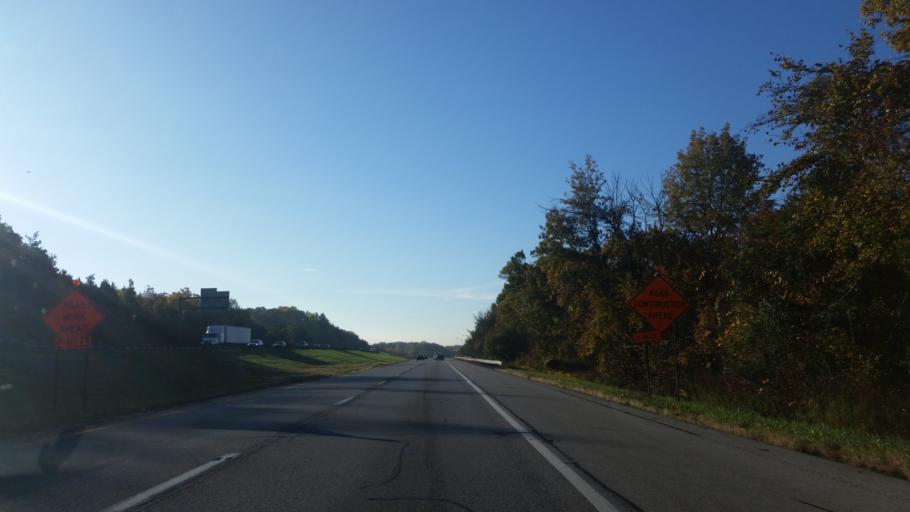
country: US
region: Ohio
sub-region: Summit County
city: Richfield
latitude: 41.2623
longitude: -81.6346
